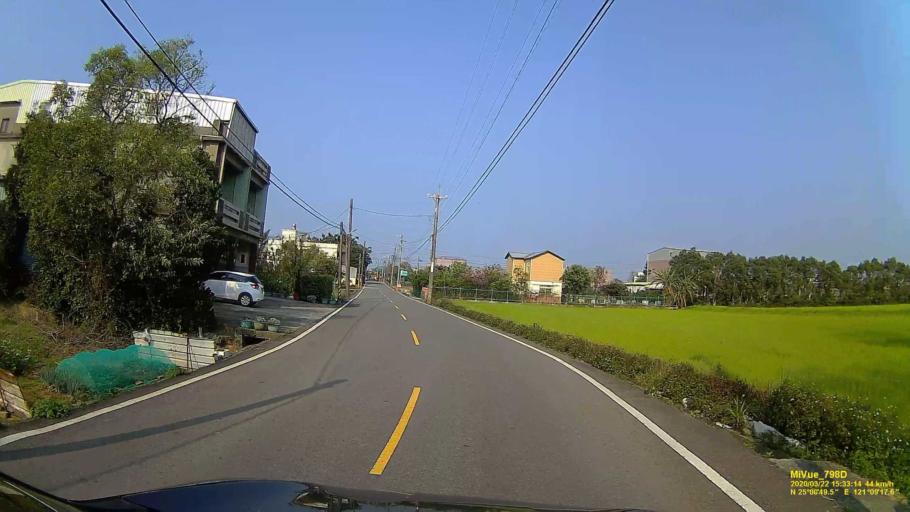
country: TW
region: Taiwan
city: Taoyuan City
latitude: 25.0139
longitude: 121.1551
